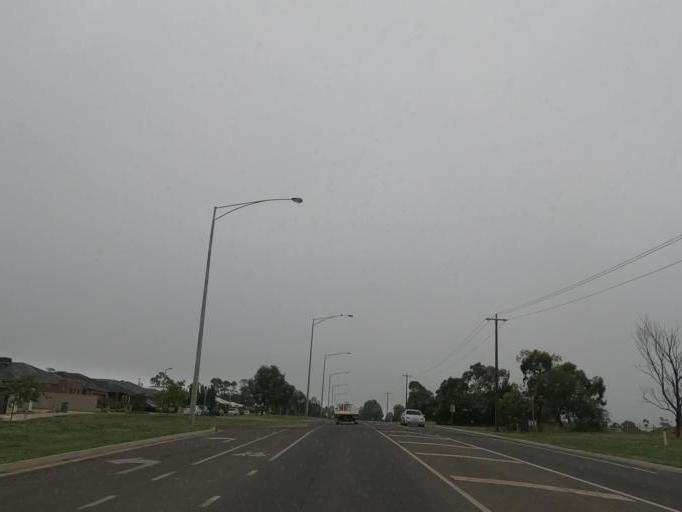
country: AU
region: Victoria
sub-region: Ballarat North
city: Newington
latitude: -37.5616
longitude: 143.8120
